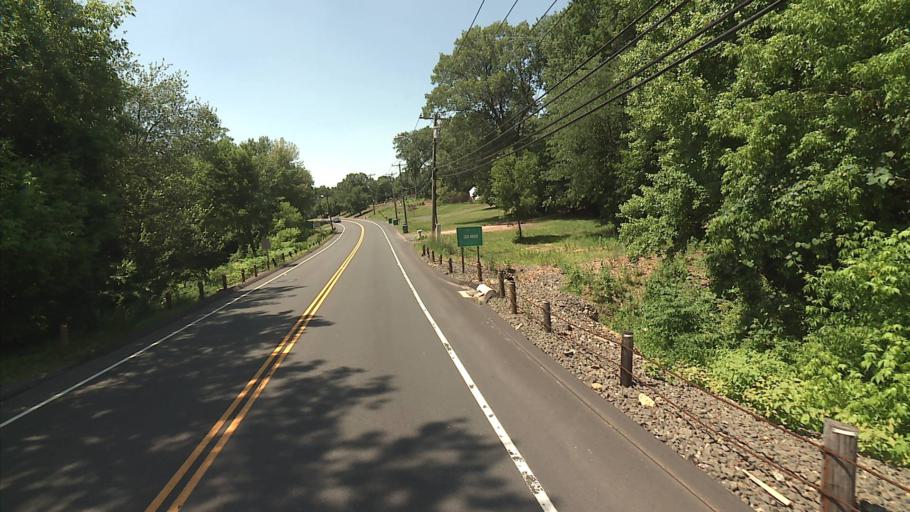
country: US
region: Connecticut
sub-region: Hartford County
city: Manchester
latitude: 41.8257
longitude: -72.5488
